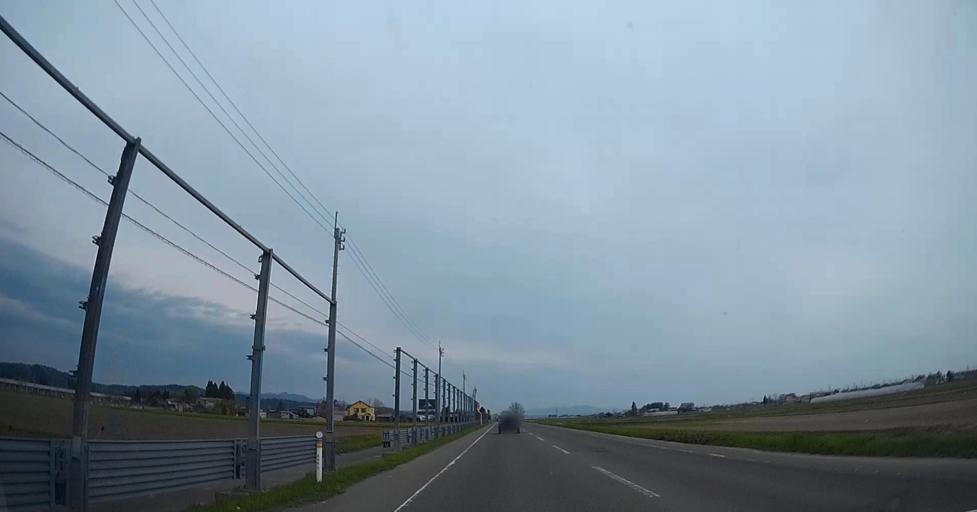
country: JP
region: Aomori
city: Aomori Shi
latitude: 40.8658
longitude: 140.6794
